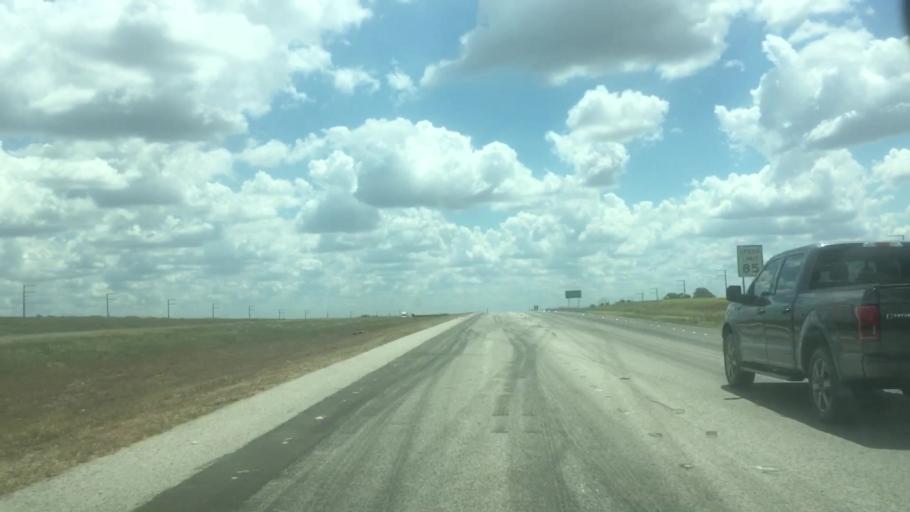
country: US
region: Texas
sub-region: Caldwell County
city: Lockhart
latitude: 29.9826
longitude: -97.6817
